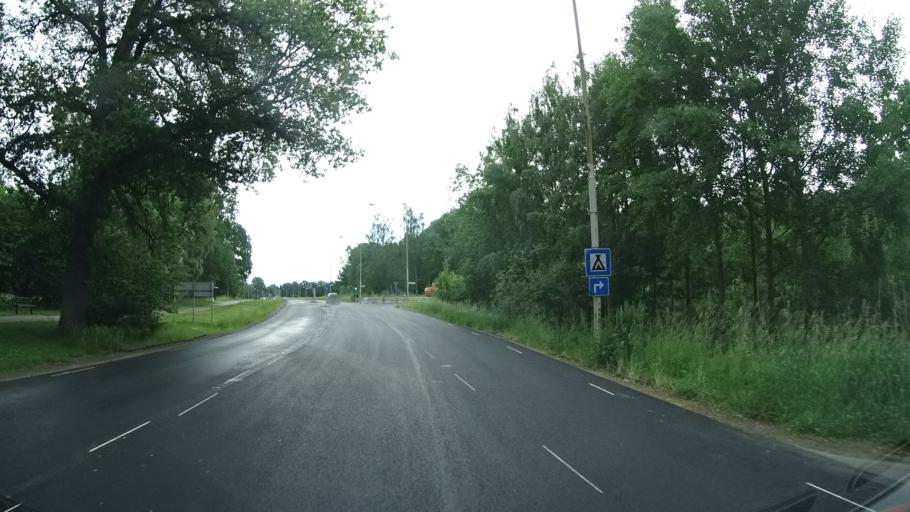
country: SE
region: OEstergoetland
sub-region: Linkopings Kommun
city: Linkoping
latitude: 58.4240
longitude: 15.5703
